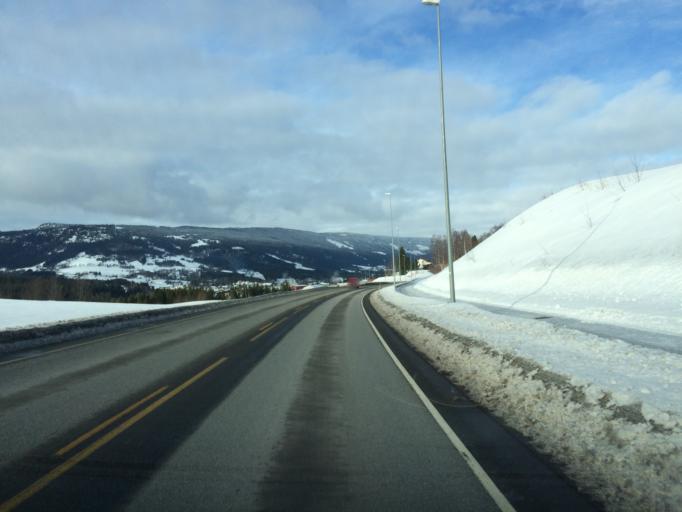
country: NO
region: Oppland
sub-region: Gausdal
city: Segalstad bru
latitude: 61.2214
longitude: 10.2416
